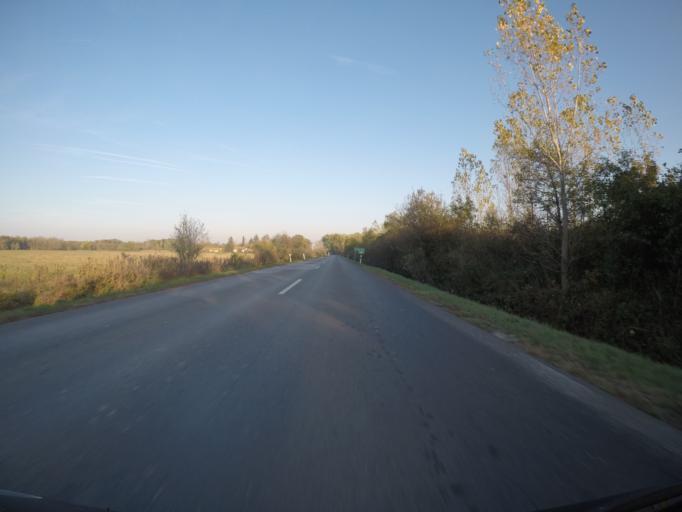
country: HU
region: Baranya
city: Szigetvar
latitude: 46.0350
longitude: 17.6984
